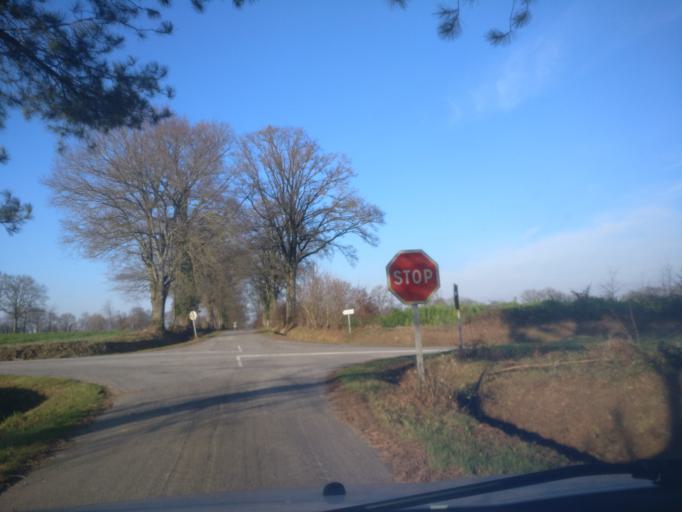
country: FR
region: Brittany
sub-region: Departement d'Ille-et-Vilaine
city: Livre-sur-Changeon
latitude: 48.1998
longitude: -1.3192
